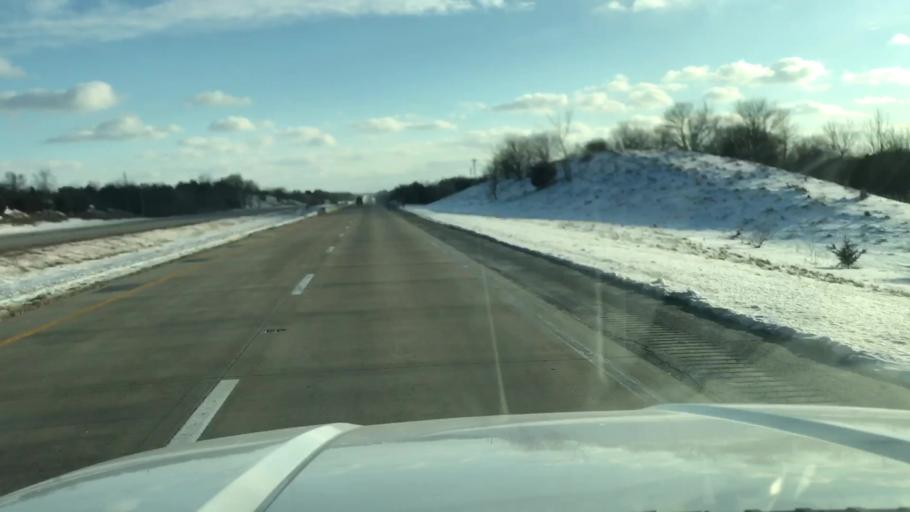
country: US
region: Missouri
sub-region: Andrew County
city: Savannah
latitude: 39.9506
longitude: -94.8603
